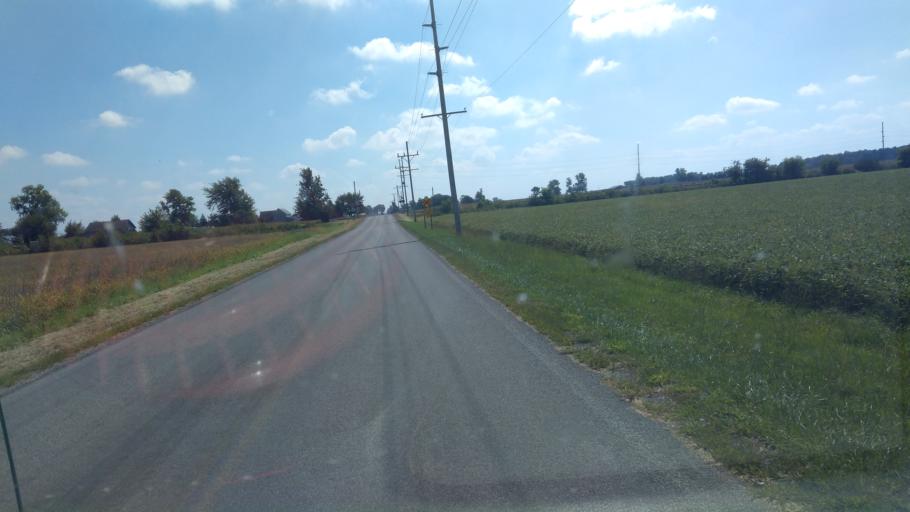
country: US
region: Ohio
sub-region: Hardin County
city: Ada
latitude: 40.7762
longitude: -83.7849
